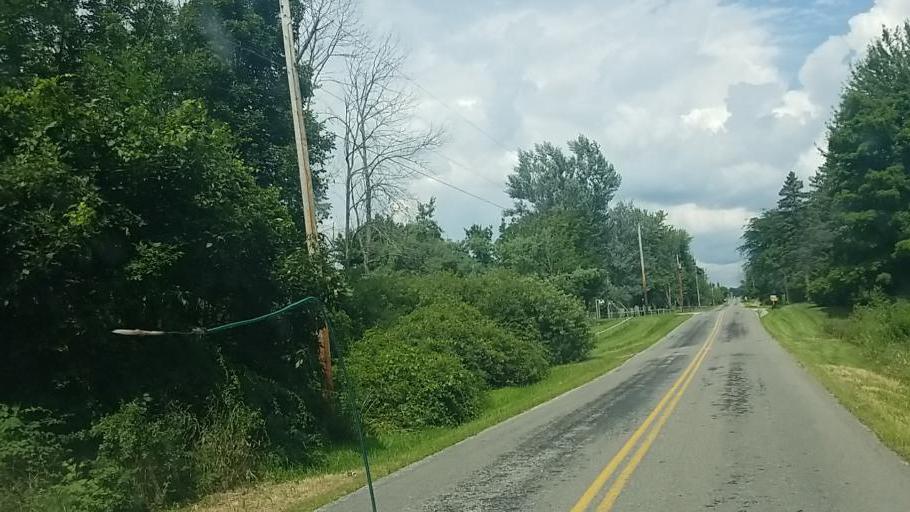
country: US
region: Ohio
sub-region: Medina County
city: Lodi
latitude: 41.1213
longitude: -82.0746
